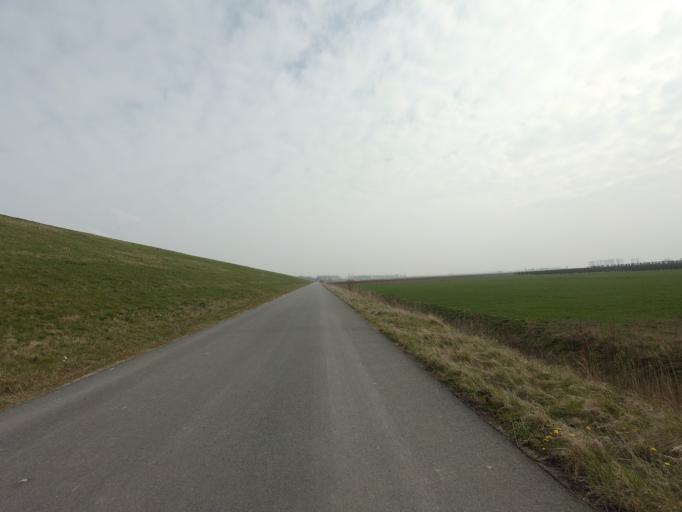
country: BE
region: Flanders
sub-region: Provincie Oost-Vlaanderen
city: Beveren
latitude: 51.3302
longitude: 4.2193
